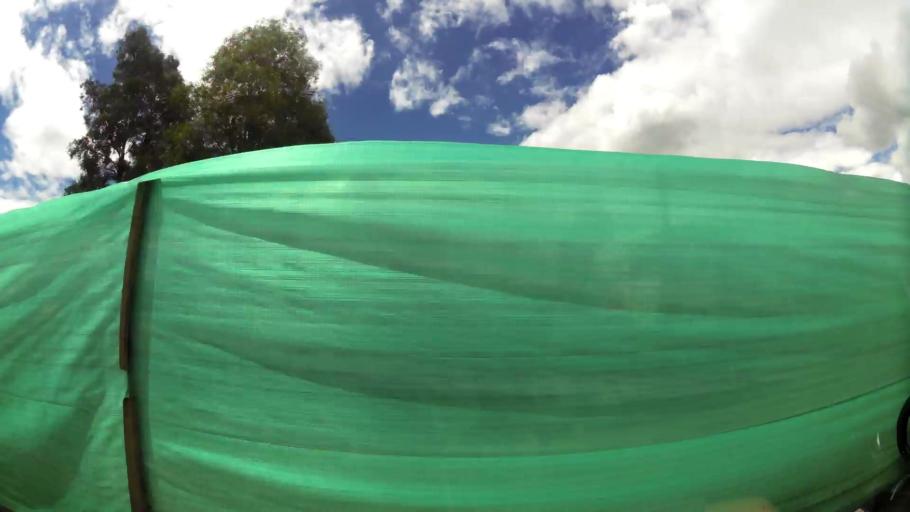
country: EC
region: Pichincha
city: Sangolqui
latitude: -0.3371
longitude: -78.5500
